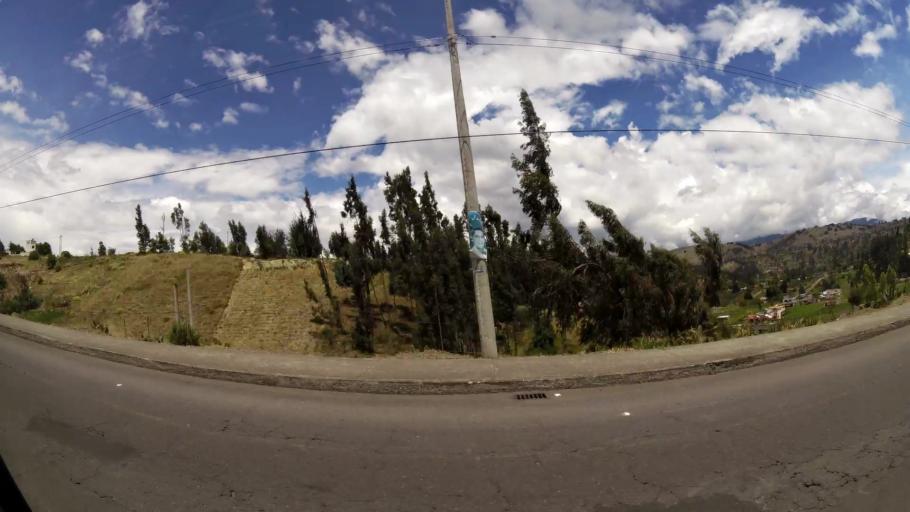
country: EC
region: Tungurahua
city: Pelileo
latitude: -1.3107
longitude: -78.5983
